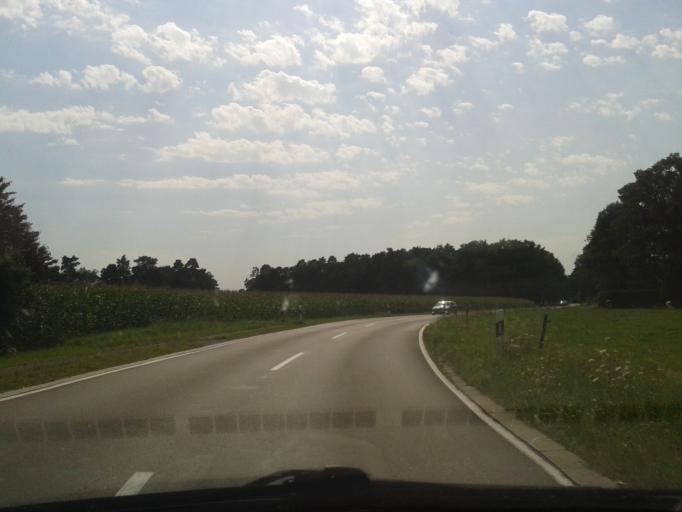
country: DE
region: North Rhine-Westphalia
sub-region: Regierungsbezirk Detmold
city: Hovelhof
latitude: 51.8792
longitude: 8.6319
